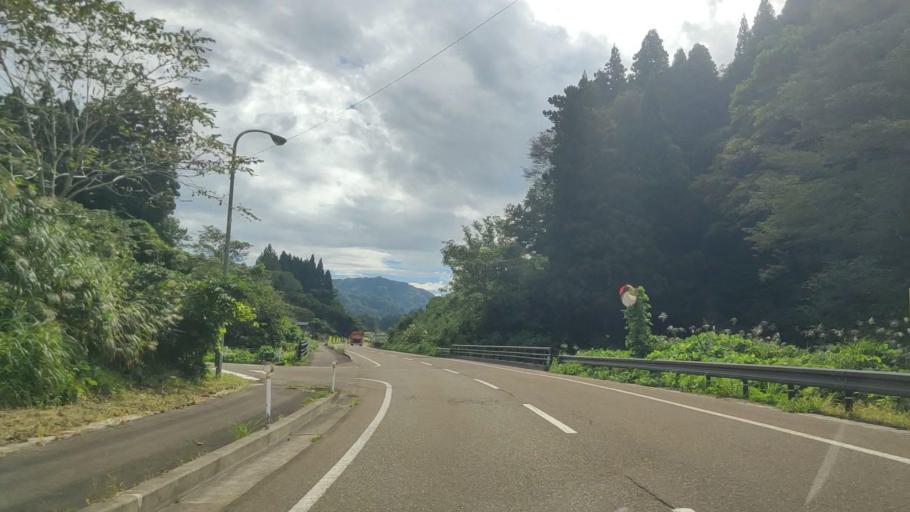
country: JP
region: Niigata
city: Arai
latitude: 36.9522
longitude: 138.2782
